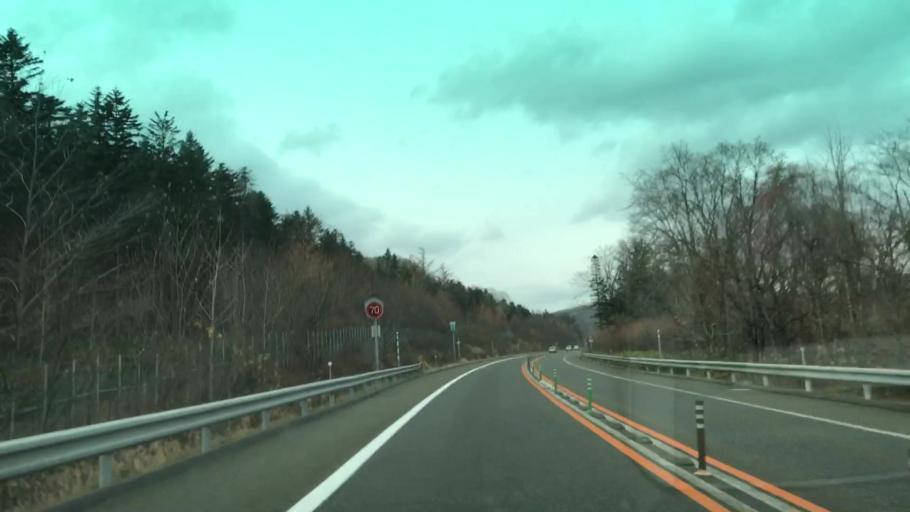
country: JP
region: Hokkaido
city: Otofuke
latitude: 43.0104
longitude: 142.8347
